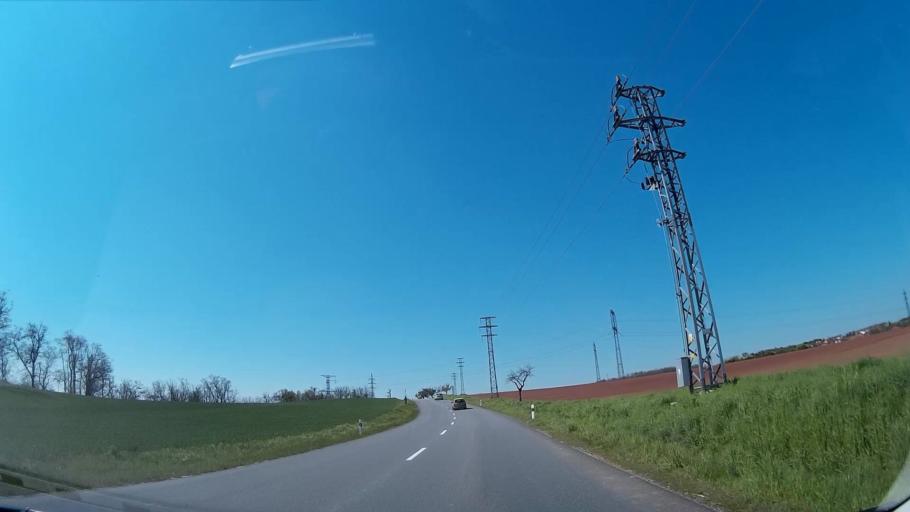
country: CZ
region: South Moravian
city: Moravsky Krumlov
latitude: 49.0697
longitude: 16.3135
